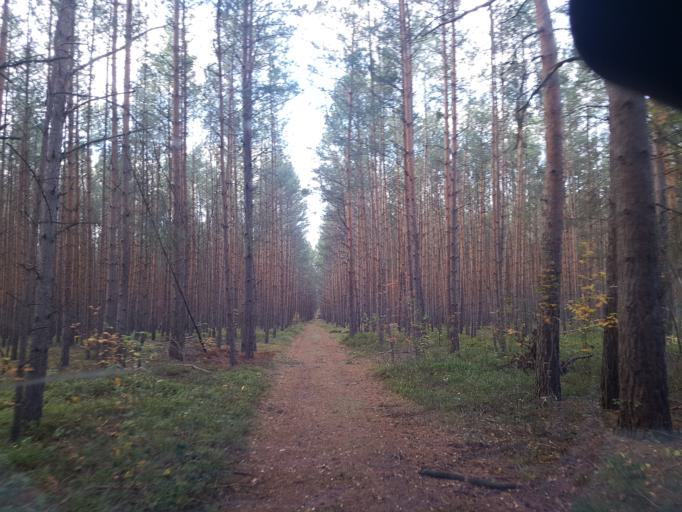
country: DE
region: Brandenburg
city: Finsterwalde
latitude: 51.5701
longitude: 13.6987
